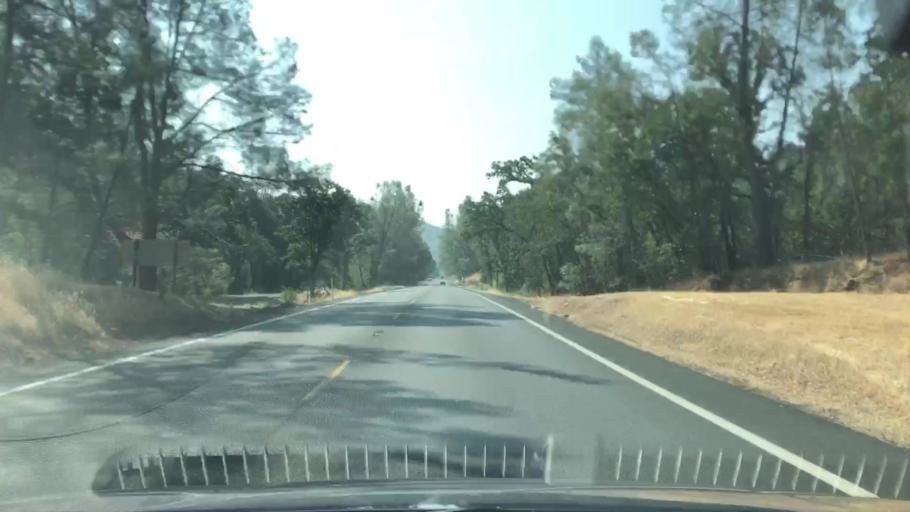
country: US
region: California
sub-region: Lake County
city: Middletown
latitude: 38.7066
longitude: -122.6074
